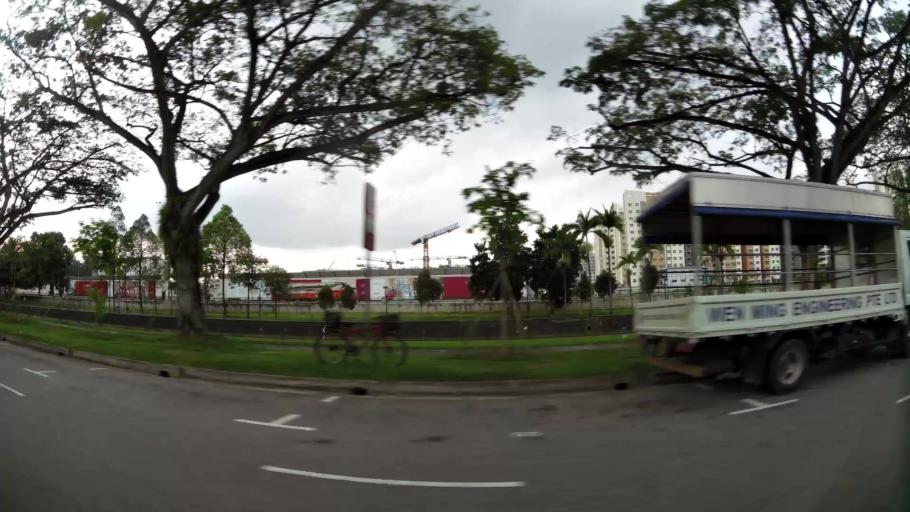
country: MY
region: Johor
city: Kampung Pasir Gudang Baru
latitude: 1.4425
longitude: 103.8322
